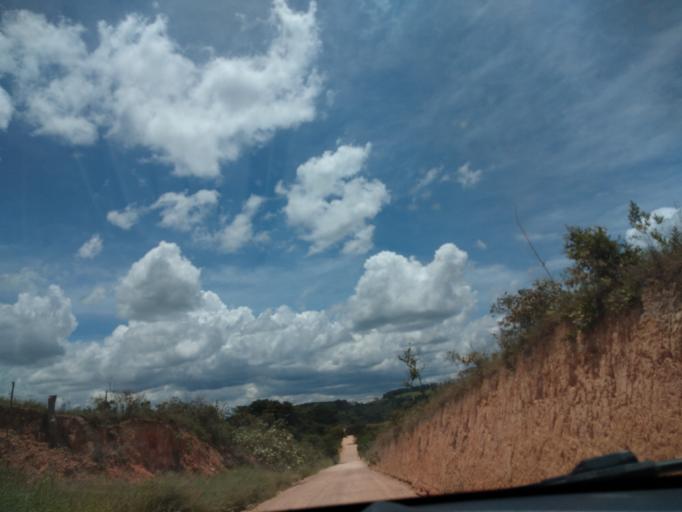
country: BR
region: Minas Gerais
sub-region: Tiradentes
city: Tiradentes
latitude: -20.9129
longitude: -44.2692
